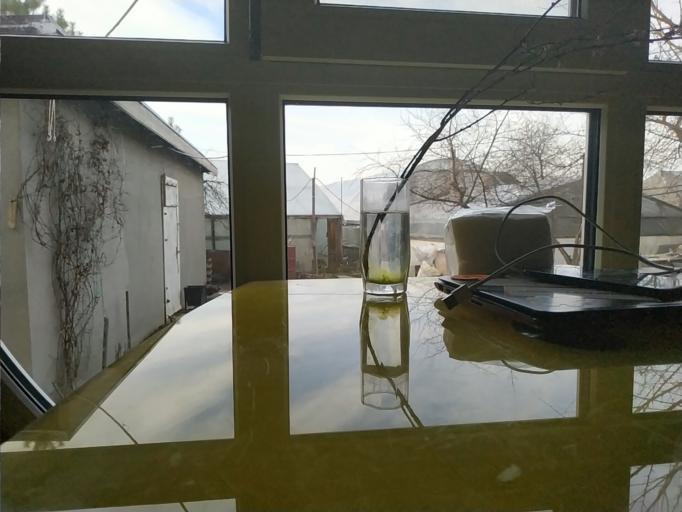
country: RU
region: Republic of Karelia
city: Suoyarvi
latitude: 61.8936
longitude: 32.2583
